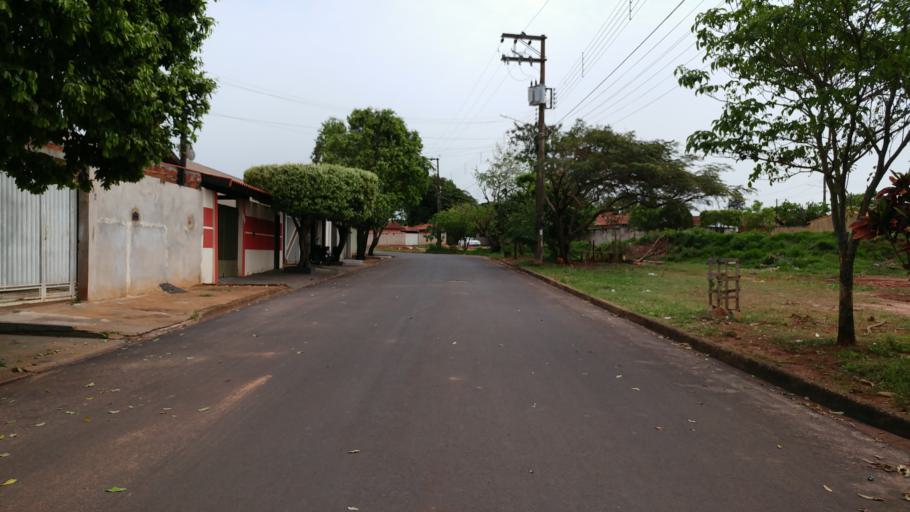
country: BR
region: Sao Paulo
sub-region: Paraguacu Paulista
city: Paraguacu Paulista
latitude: -22.4371
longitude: -50.5822
